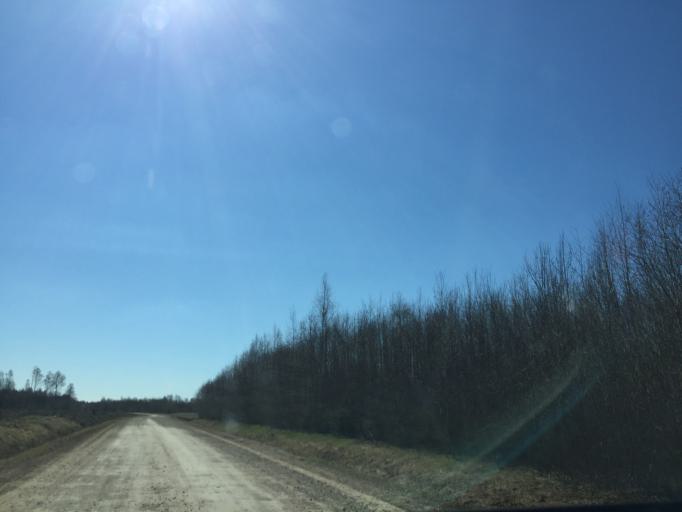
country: EE
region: Viljandimaa
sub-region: Viiratsi vald
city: Viiratsi
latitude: 58.4036
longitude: 25.8711
